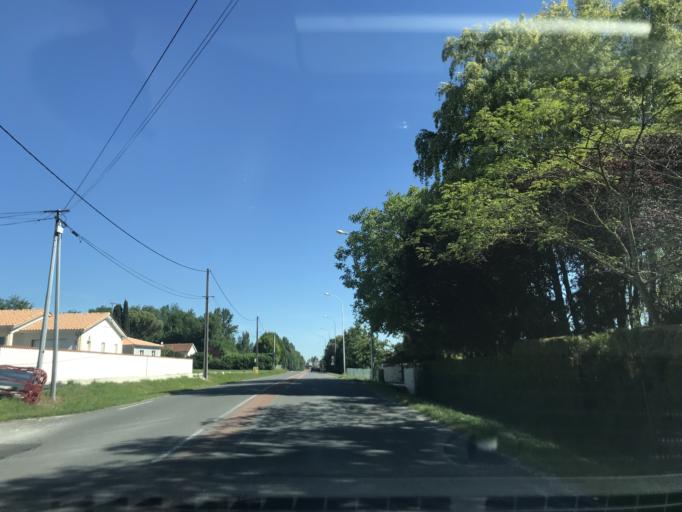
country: FR
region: Poitou-Charentes
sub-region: Departement de la Charente
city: Barbezieux-Saint-Hilaire
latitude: 45.4631
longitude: -0.1519
